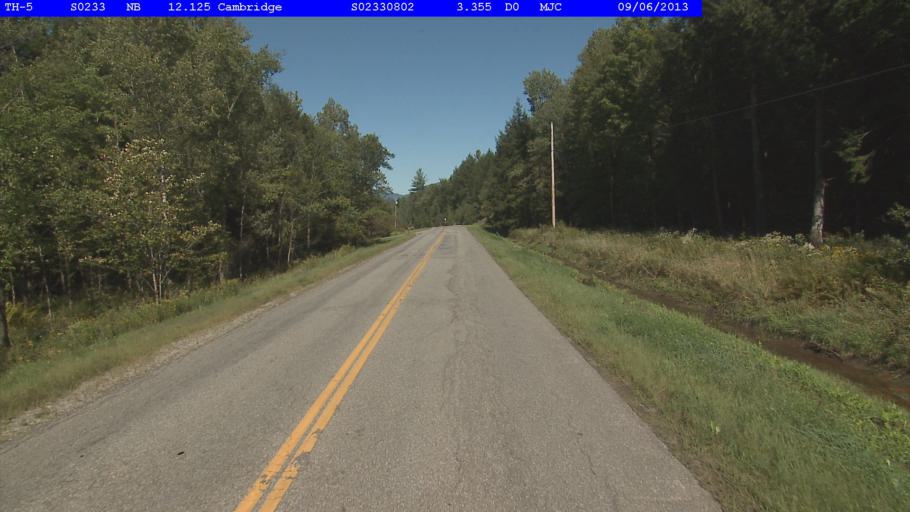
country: US
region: Vermont
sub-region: Lamoille County
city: Johnson
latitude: 44.6284
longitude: -72.8490
